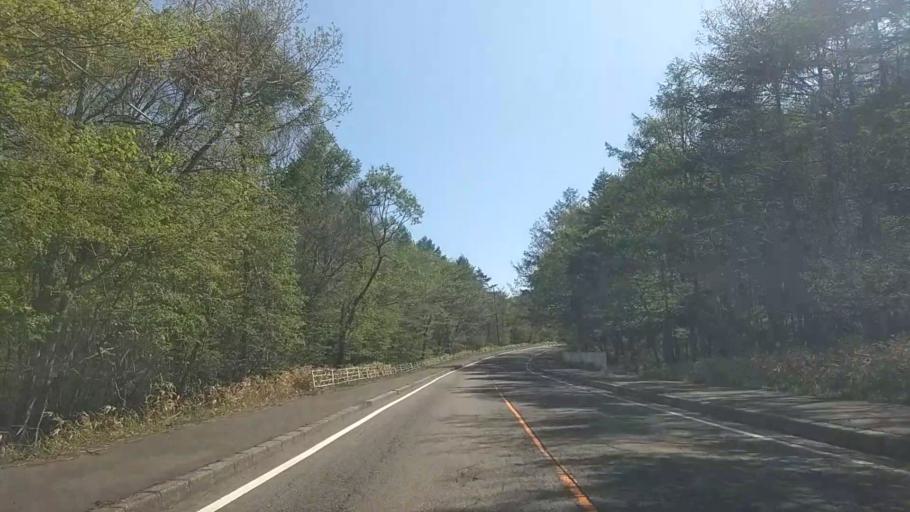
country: JP
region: Yamanashi
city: Nirasaki
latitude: 35.9405
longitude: 138.4343
